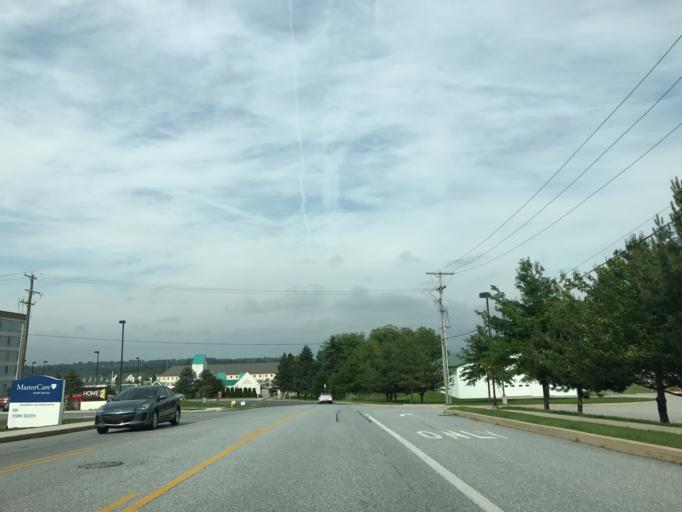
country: US
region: Pennsylvania
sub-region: York County
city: Spry
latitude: 39.9314
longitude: -76.6851
